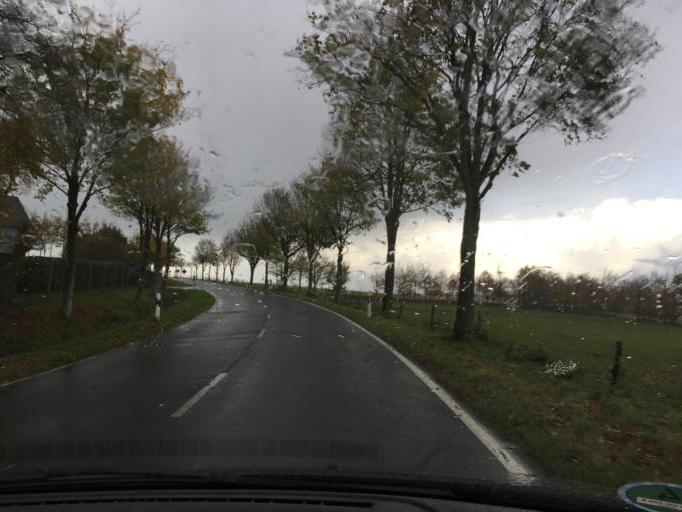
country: DE
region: North Rhine-Westphalia
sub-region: Regierungsbezirk Koln
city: Simmerath
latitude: 50.6324
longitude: 6.3498
